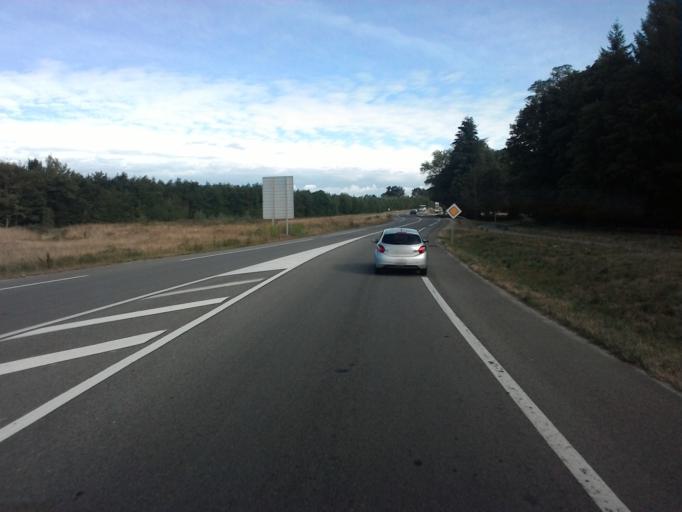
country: FR
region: Rhone-Alpes
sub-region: Departement de l'Ain
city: Montagnat
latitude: 46.1668
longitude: 5.2638
